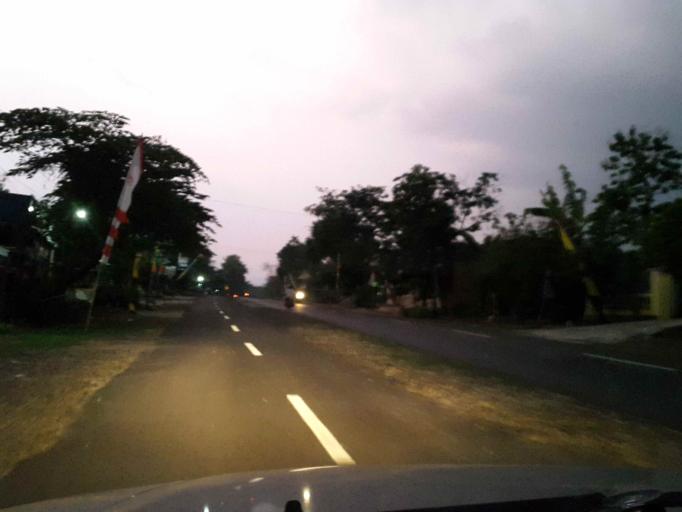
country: ID
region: Central Java
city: Jaten
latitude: -7.6182
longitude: 111.0127
